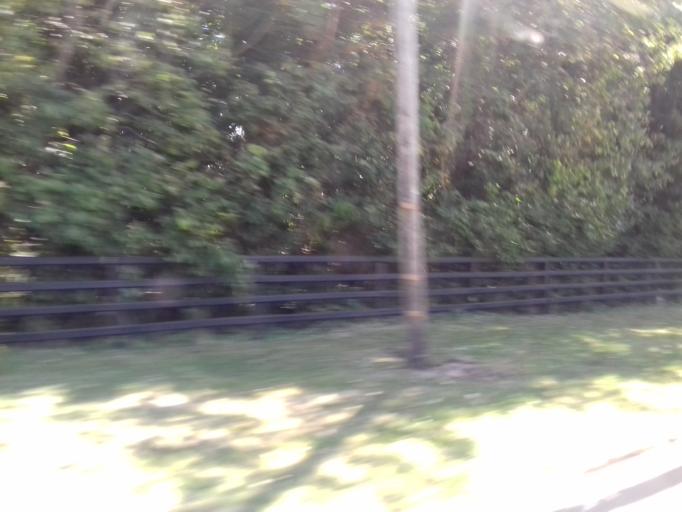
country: IE
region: Leinster
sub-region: Fingal County
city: Swords
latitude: 53.5055
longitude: -6.2676
